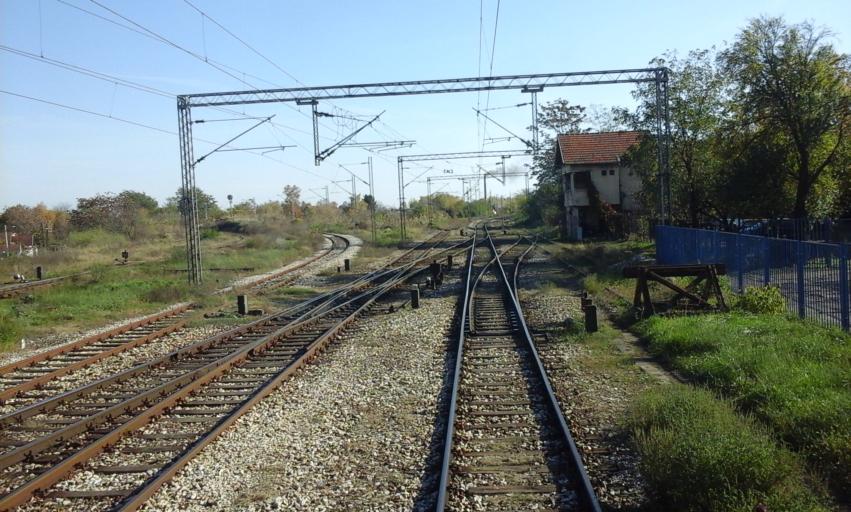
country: RS
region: Autonomna Pokrajina Vojvodina
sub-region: Severnobacki Okrug
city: Subotica
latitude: 46.0933
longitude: 19.6798
